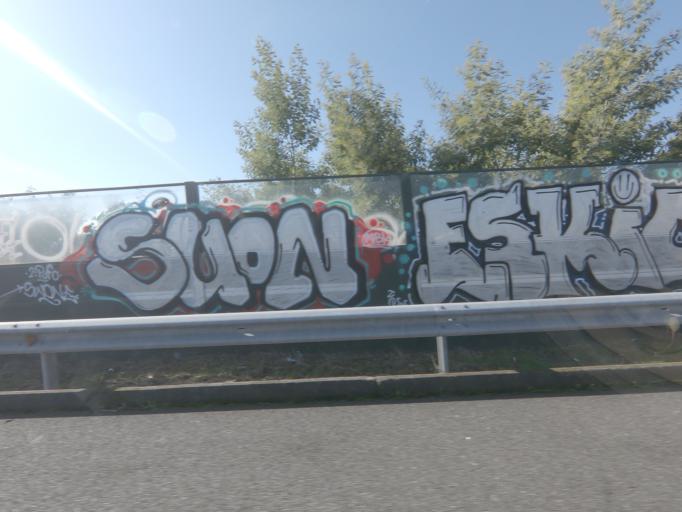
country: ES
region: Galicia
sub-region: Provincia de Ourense
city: Punxin
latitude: 42.3504
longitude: -7.9969
